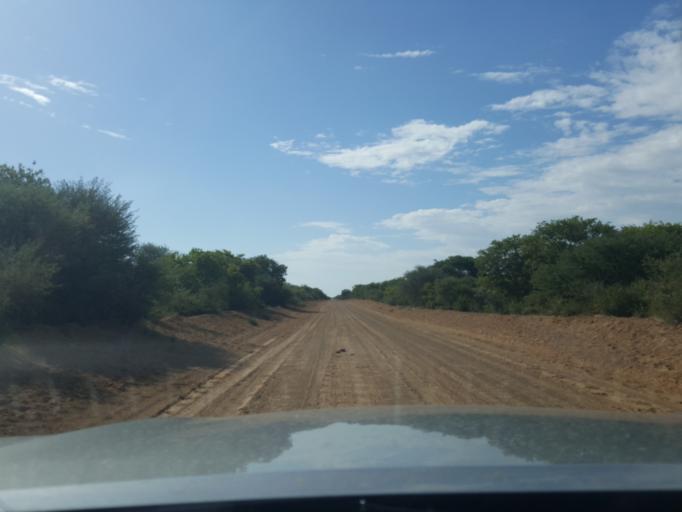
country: BW
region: Kweneng
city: Khudumelapye
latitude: -23.5144
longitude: 24.7151
